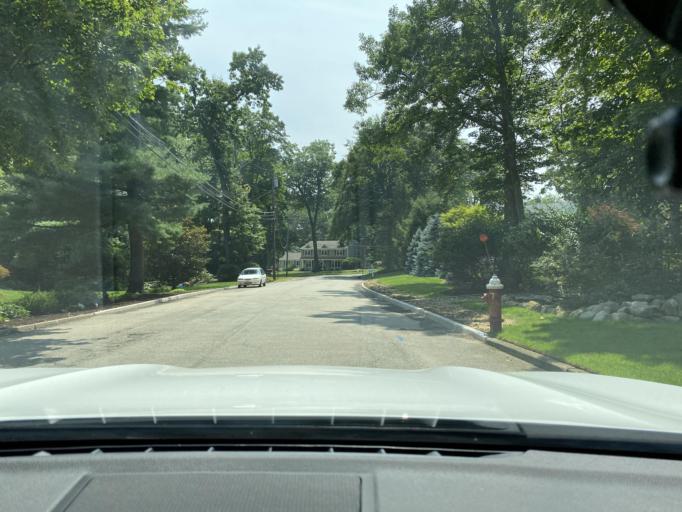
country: US
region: New York
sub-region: Rockland County
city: Airmont
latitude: 41.0820
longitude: -74.1071
